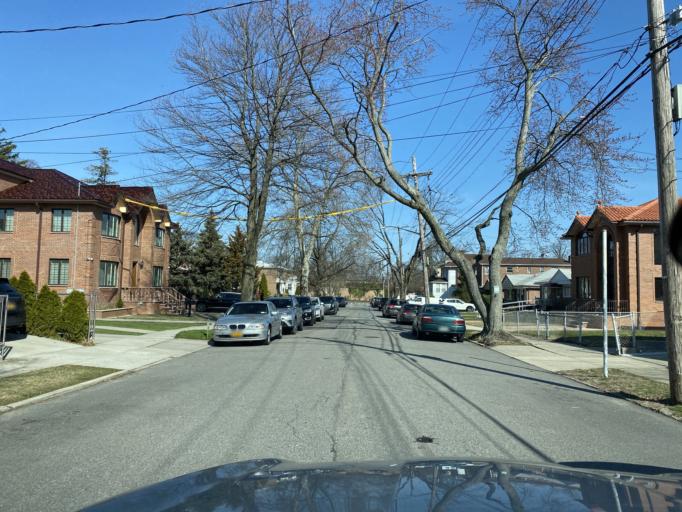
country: US
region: New York
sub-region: Nassau County
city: Bellerose Terrace
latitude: 40.7497
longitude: -73.7479
